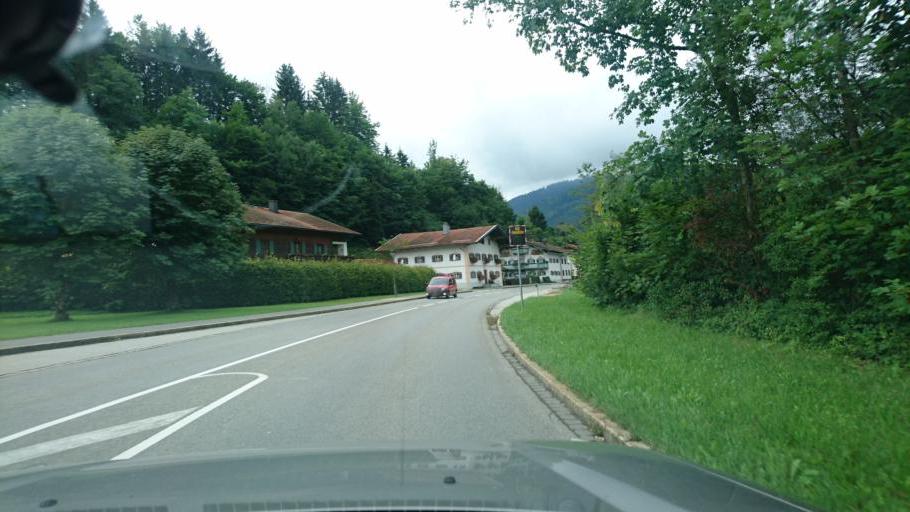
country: DE
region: Bavaria
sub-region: Upper Bavaria
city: Siegsdorf
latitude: 47.8011
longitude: 12.6434
